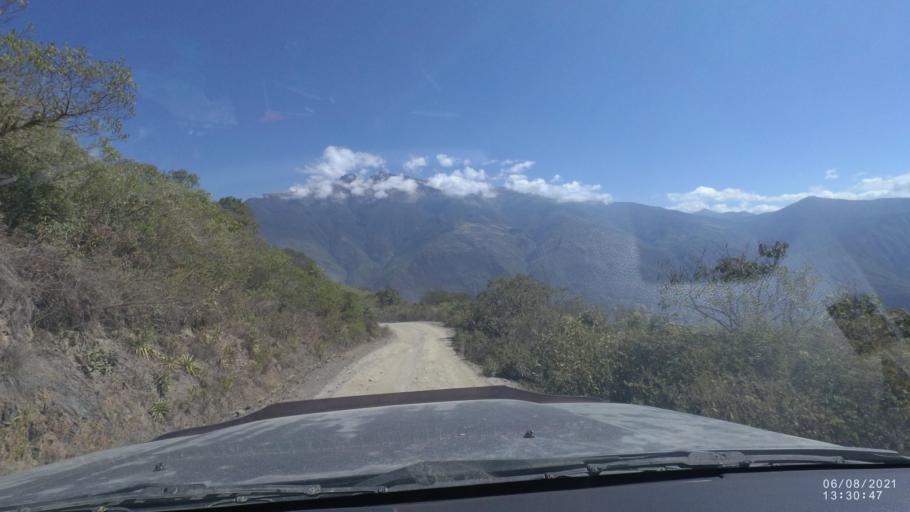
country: BO
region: La Paz
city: Quime
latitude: -16.7004
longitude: -66.7246
